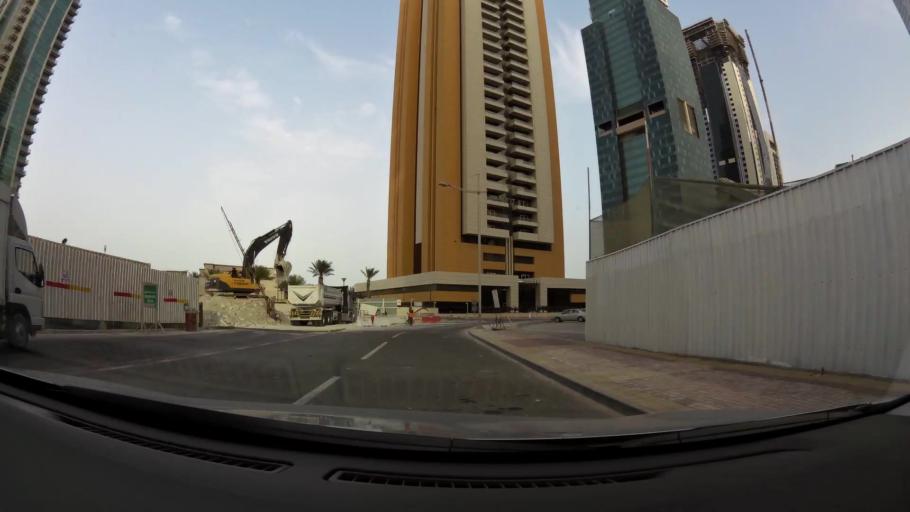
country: QA
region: Baladiyat ad Dawhah
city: Doha
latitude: 25.3297
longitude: 51.5347
